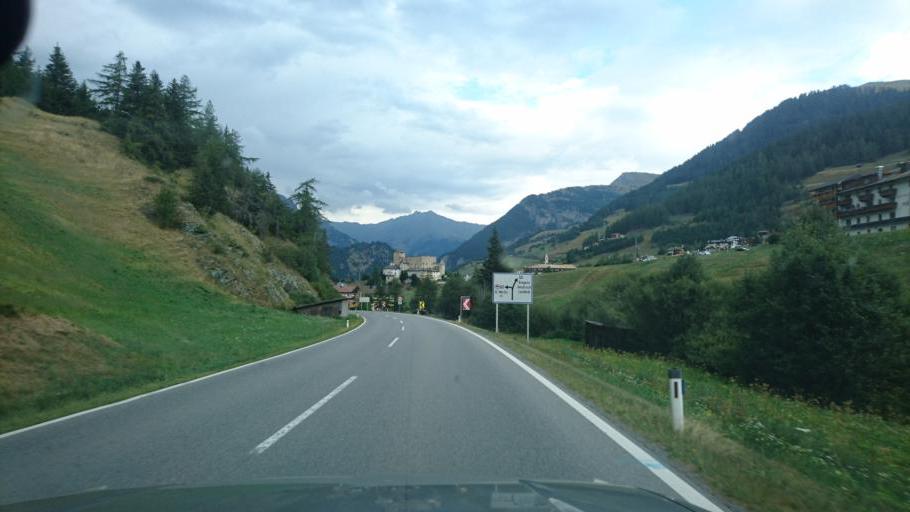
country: AT
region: Tyrol
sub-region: Politischer Bezirk Landeck
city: Nauders
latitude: 46.8827
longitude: 10.5052
